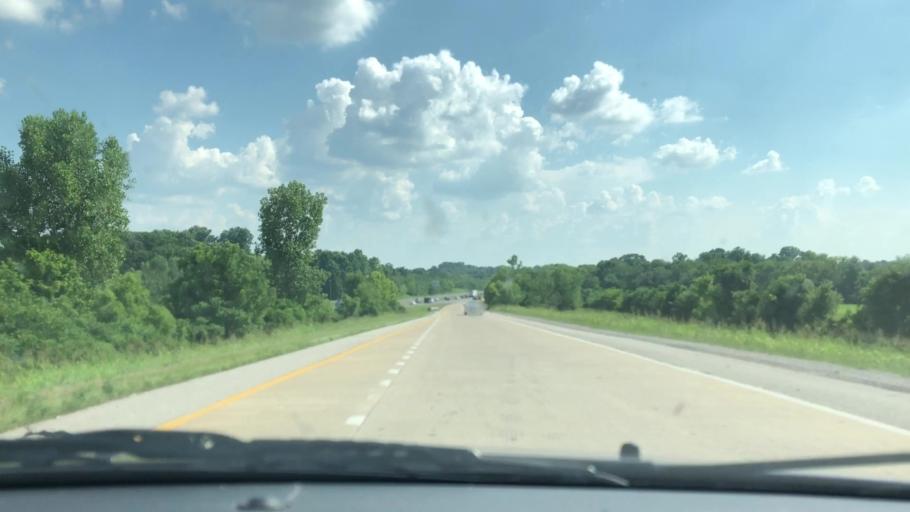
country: US
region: Tennessee
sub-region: Williamson County
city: Thompson's Station
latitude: 35.8144
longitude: -86.8450
